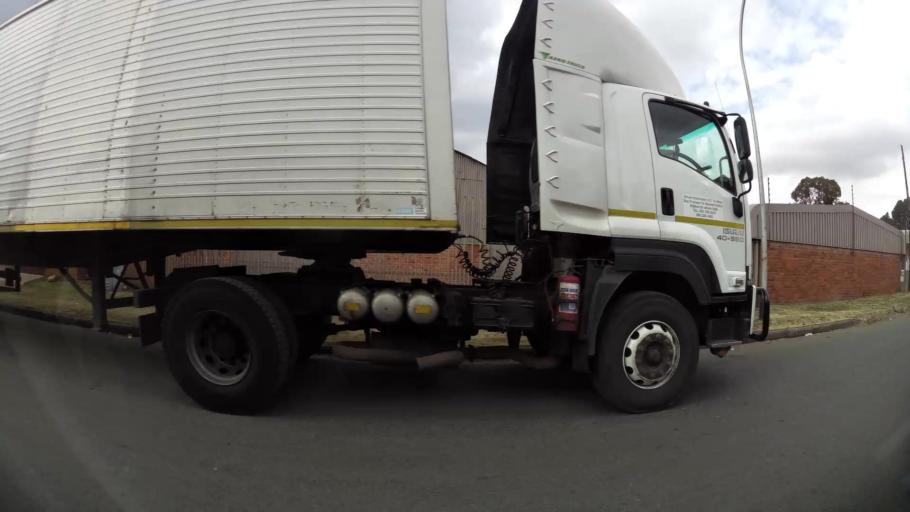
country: ZA
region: Orange Free State
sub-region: Mangaung Metropolitan Municipality
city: Bloemfontein
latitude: -29.1256
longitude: 26.2265
